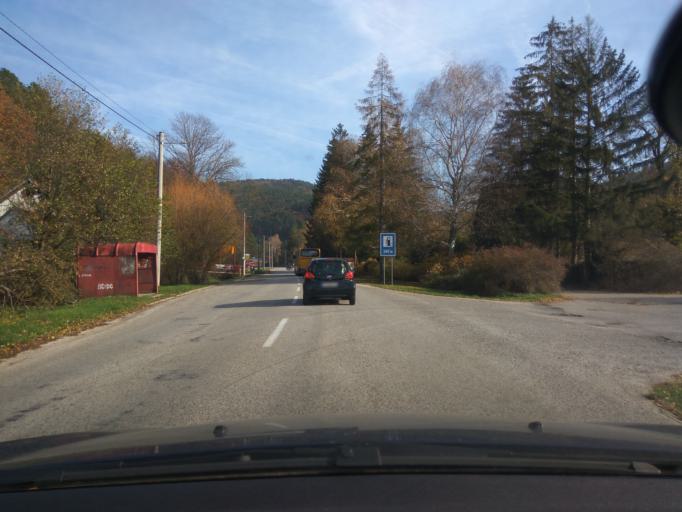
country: SK
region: Nitriansky
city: Brezova pod Bradlom
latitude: 48.6521
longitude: 17.5298
